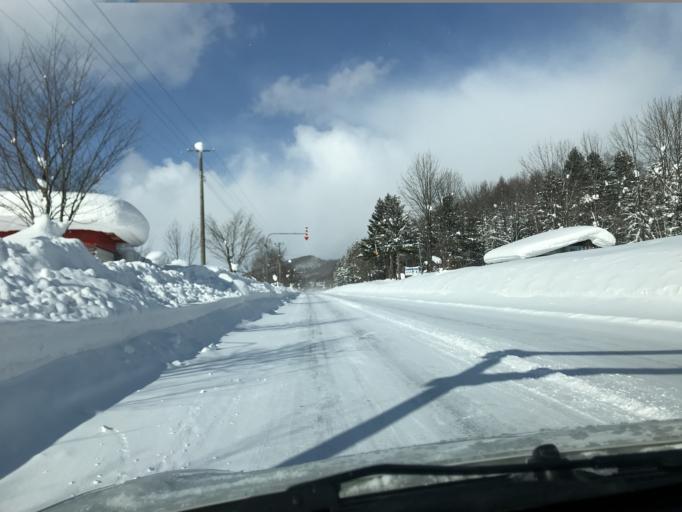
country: JP
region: Hokkaido
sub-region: Asahikawa-shi
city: Asahikawa
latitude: 43.9284
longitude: 142.4733
